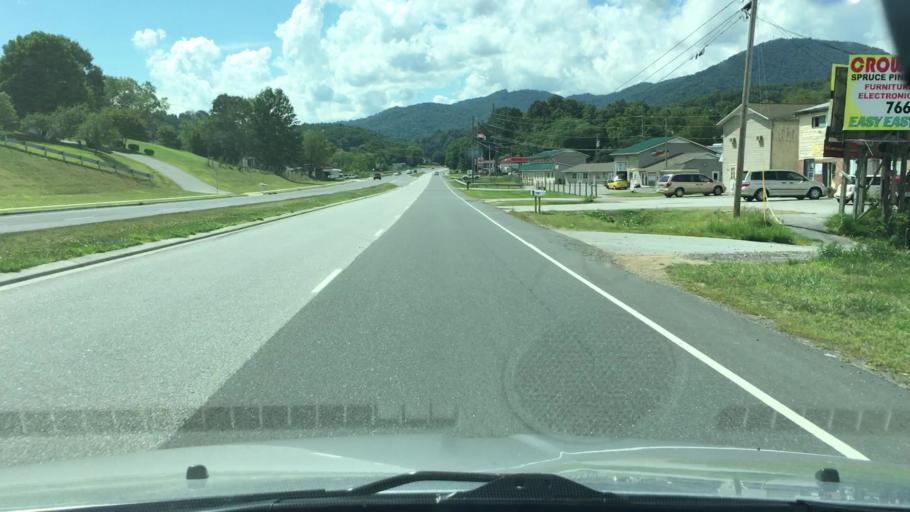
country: US
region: North Carolina
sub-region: Yancey County
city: Burnsville
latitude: 35.9143
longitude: -82.2630
